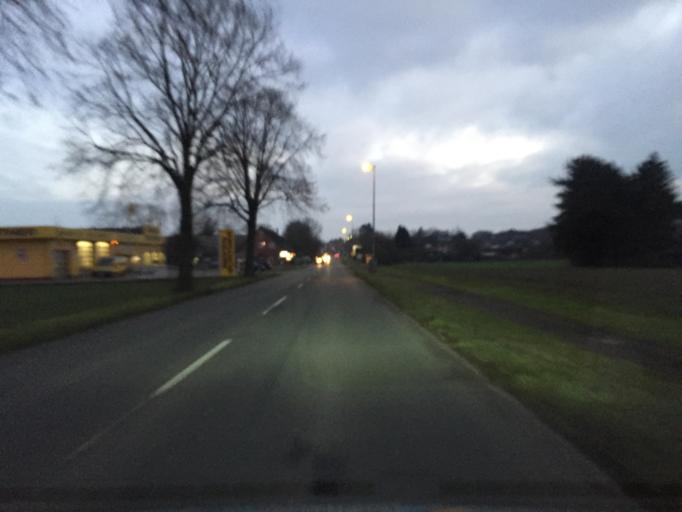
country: DE
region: Lower Saxony
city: Sulingen
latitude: 52.6765
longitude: 8.7896
